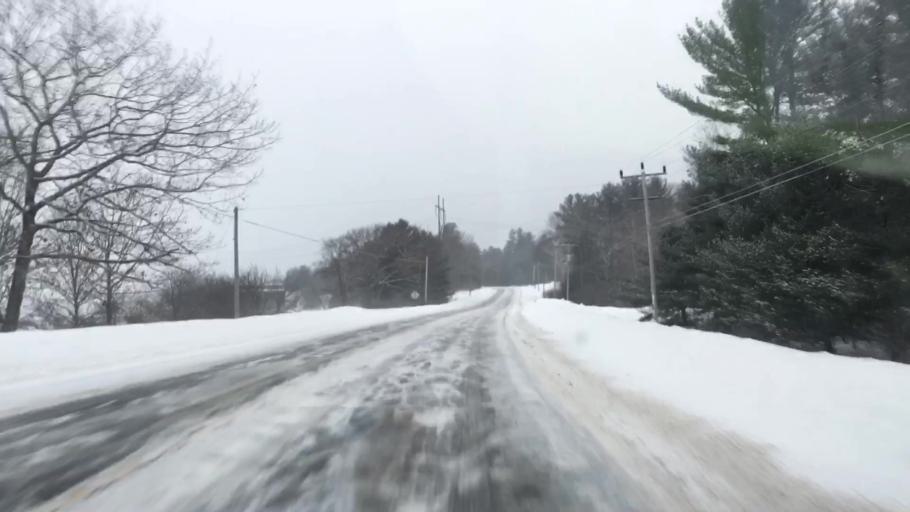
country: US
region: Maine
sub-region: Penobscot County
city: Medway
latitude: 45.5667
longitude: -68.4016
